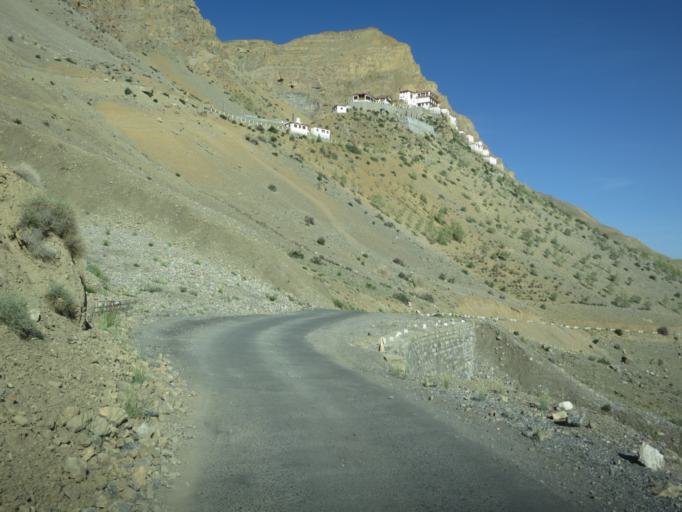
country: IN
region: Himachal Pradesh
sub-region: Shimla
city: Sarahan
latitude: 32.2997
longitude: 78.0082
